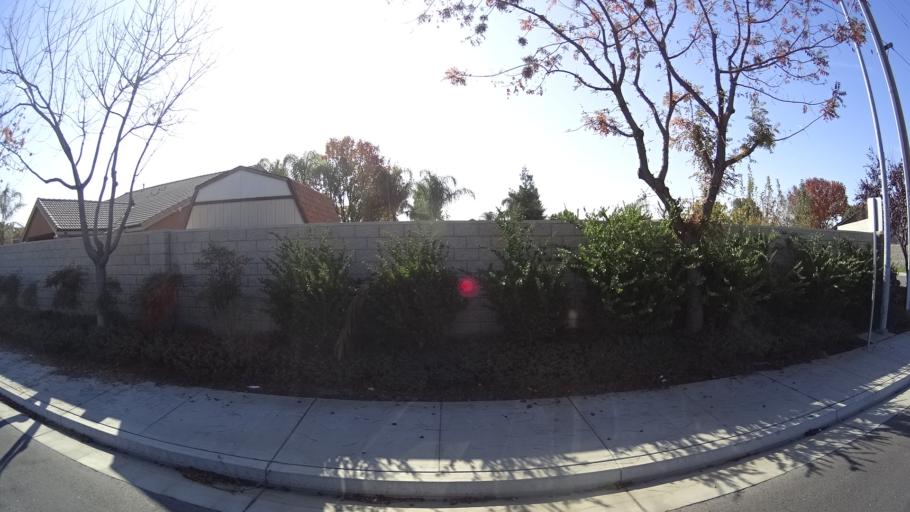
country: US
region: California
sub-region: Kern County
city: Greenfield
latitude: 35.2742
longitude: -119.0592
